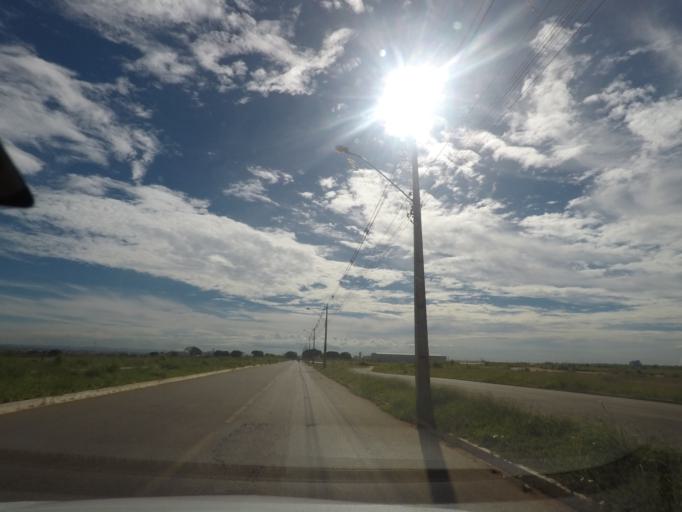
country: BR
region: Goias
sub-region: Aparecida De Goiania
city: Aparecida de Goiania
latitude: -16.8093
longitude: -49.2760
